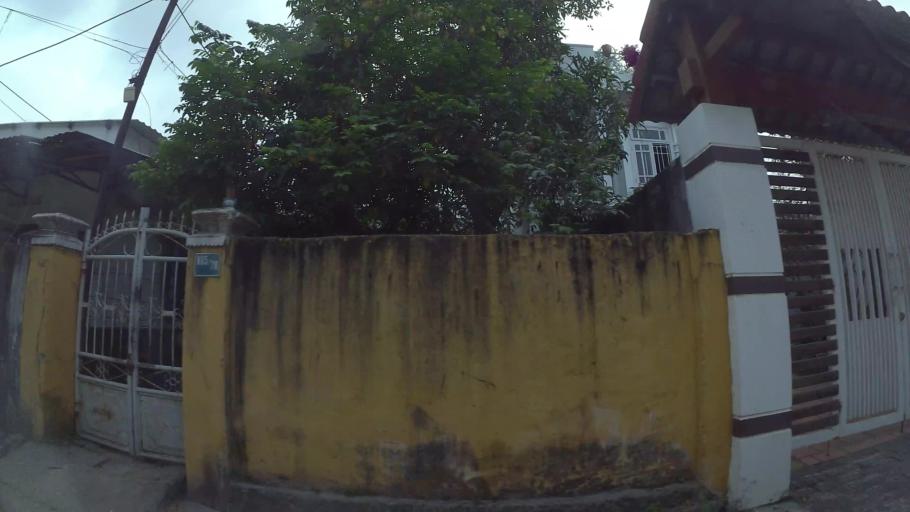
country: VN
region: Da Nang
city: Son Tra
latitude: 16.0597
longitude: 108.2444
